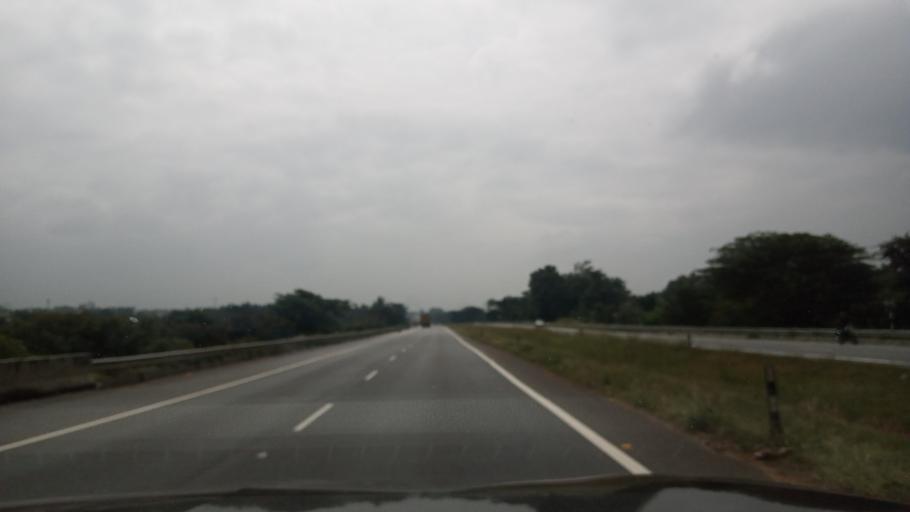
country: IN
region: Karnataka
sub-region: Bangalore Urban
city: Bangalore
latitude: 12.9411
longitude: 77.4696
